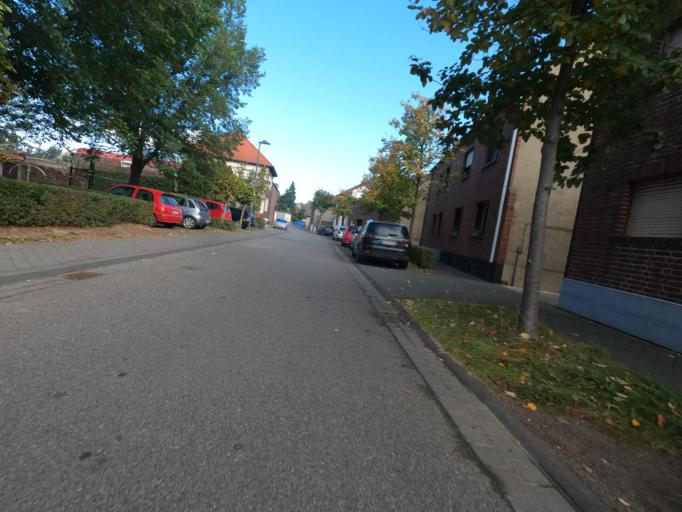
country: DE
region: North Rhine-Westphalia
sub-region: Regierungsbezirk Koln
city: Inden
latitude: 50.8789
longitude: 6.3973
